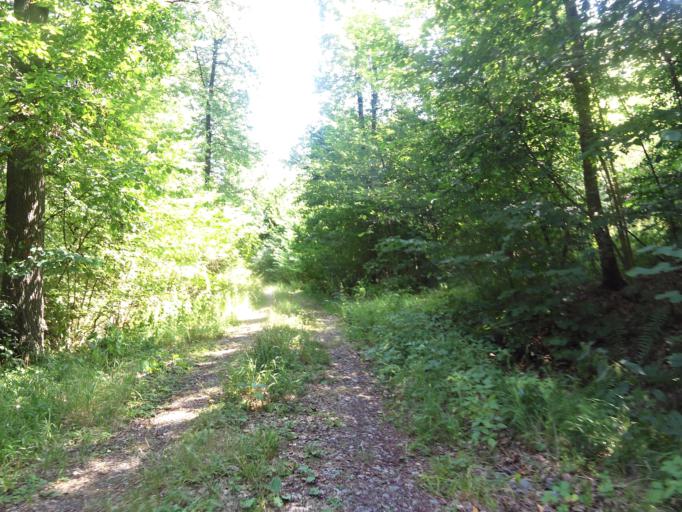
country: DE
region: Bavaria
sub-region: Regierungsbezirk Unterfranken
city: Rimpar
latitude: 49.8295
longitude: 9.9452
